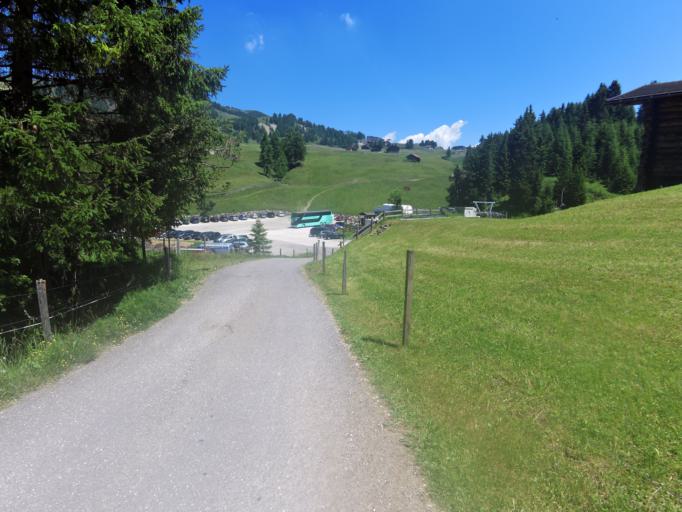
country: IT
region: Trentino-Alto Adige
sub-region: Bolzano
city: Siusi
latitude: 46.5372
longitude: 11.6046
